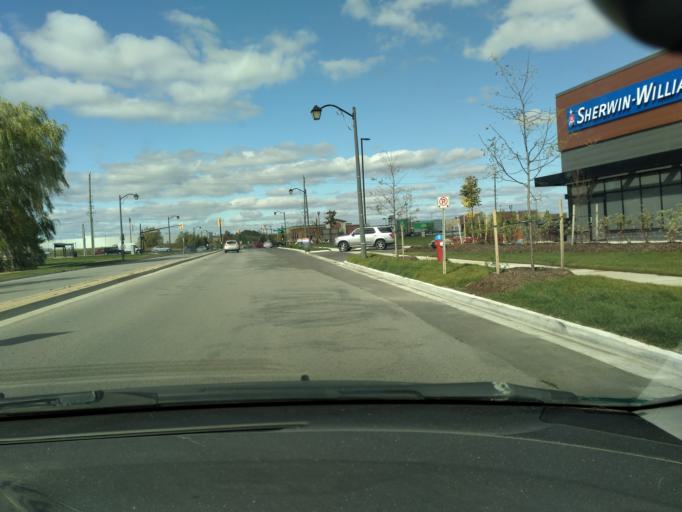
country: CA
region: Ontario
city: Bradford West Gwillimbury
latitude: 44.1065
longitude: -79.5937
